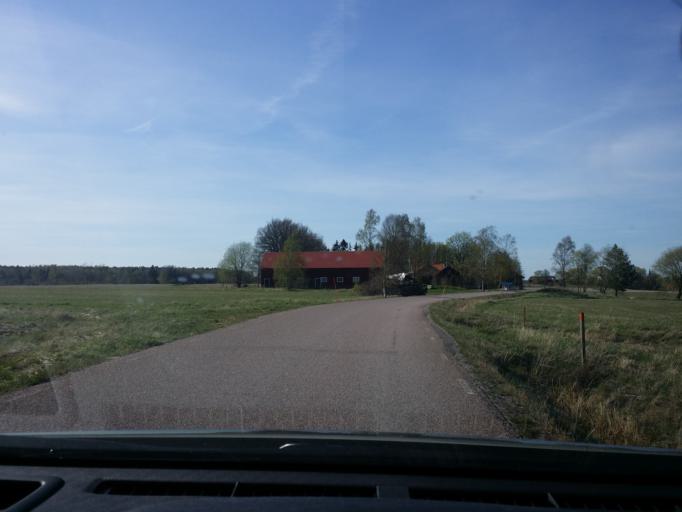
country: SE
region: Vaestmanland
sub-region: Vasteras
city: Vasteras
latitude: 59.6353
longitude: 16.4864
